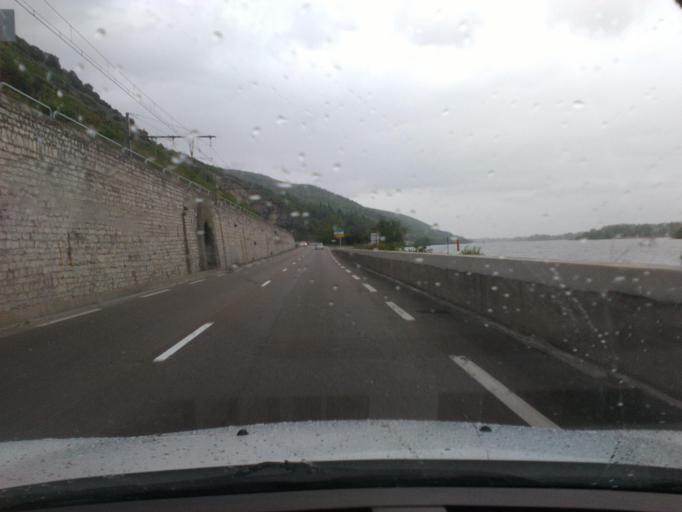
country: FR
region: Rhone-Alpes
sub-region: Departement de l'Ardeche
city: Le Pouzin
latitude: 44.7652
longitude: 4.7529
